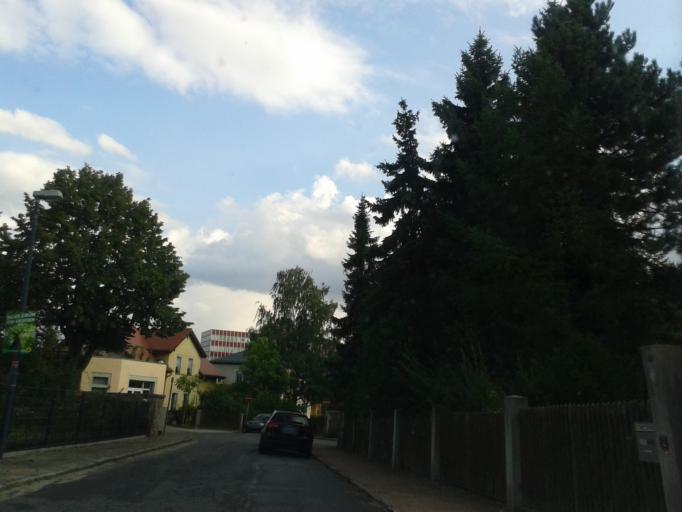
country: DE
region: Saxony
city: Radebeul
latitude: 51.1048
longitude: 13.6812
